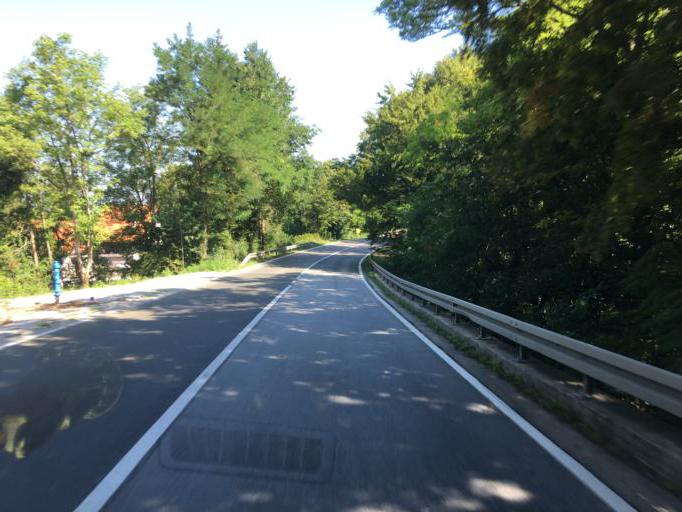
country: HR
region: Karlovacka
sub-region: Grad Karlovac
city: Slunj
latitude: 45.2475
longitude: 15.5510
